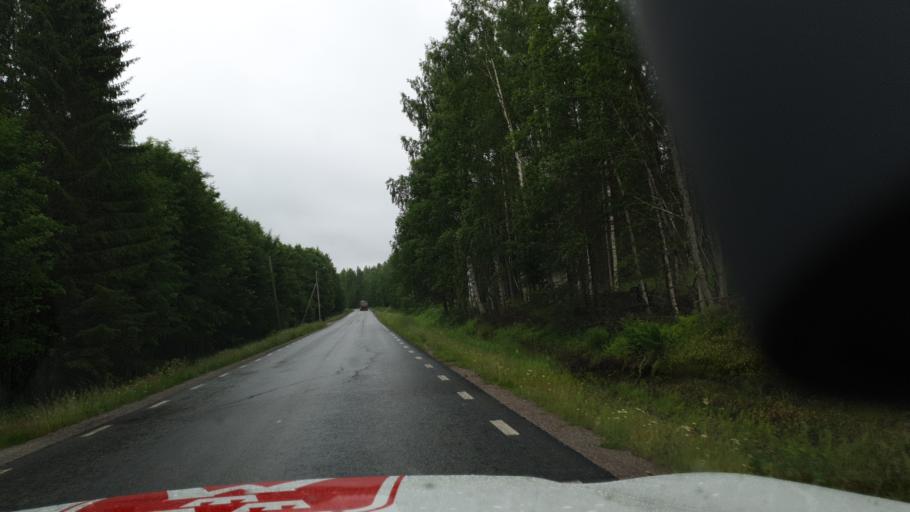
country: SE
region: Vaesterbotten
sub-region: Vannas Kommun
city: Vannasby
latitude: 63.8394
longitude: 19.8627
